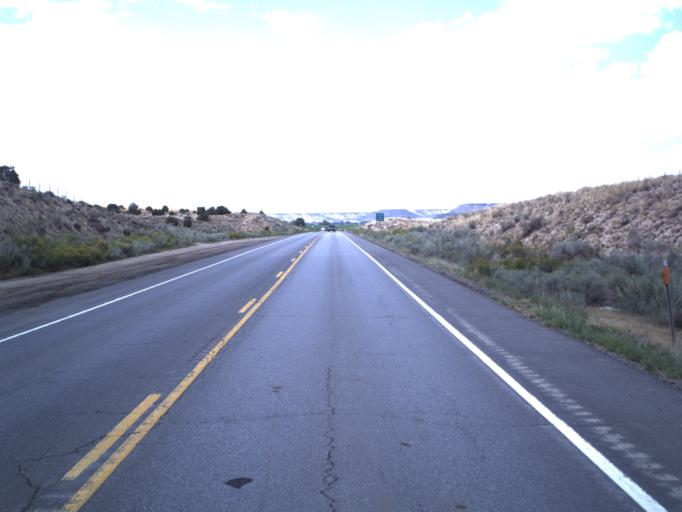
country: US
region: Utah
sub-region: Duchesne County
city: Duchesne
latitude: 40.1671
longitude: -110.2935
